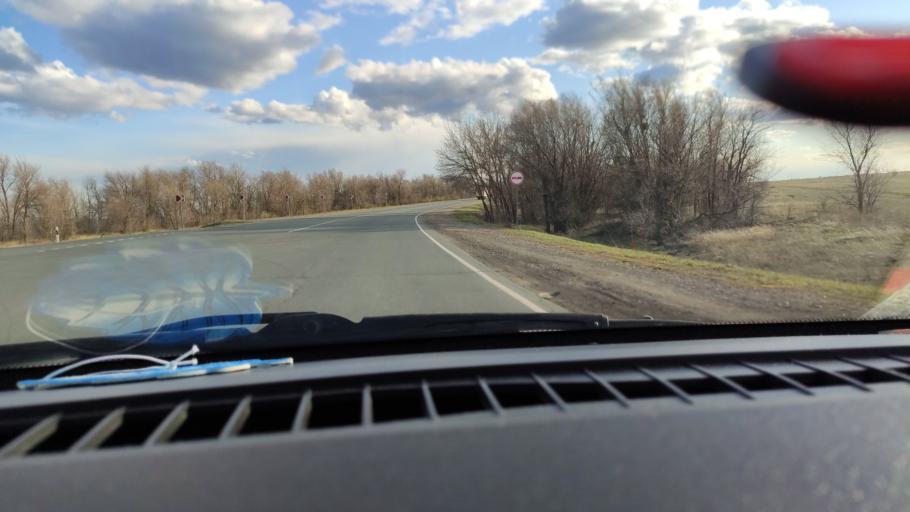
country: RU
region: Saratov
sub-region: Saratovskiy Rayon
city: Saratov
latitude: 51.7123
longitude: 46.0210
